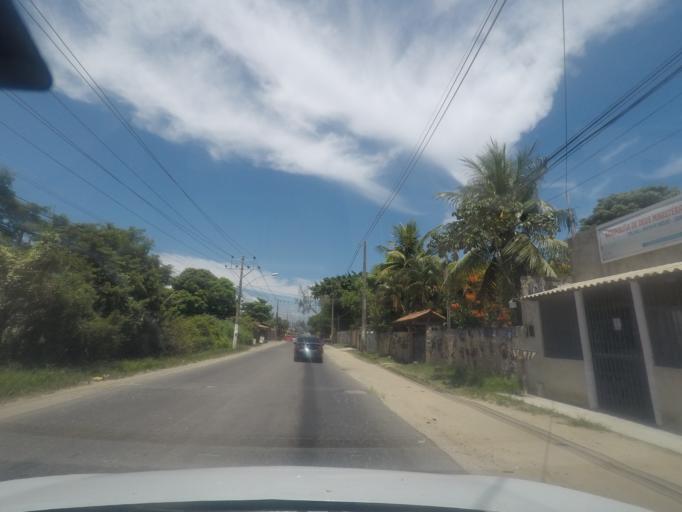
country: BR
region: Rio de Janeiro
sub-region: Itaguai
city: Itaguai
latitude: -22.9781
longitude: -43.6788
